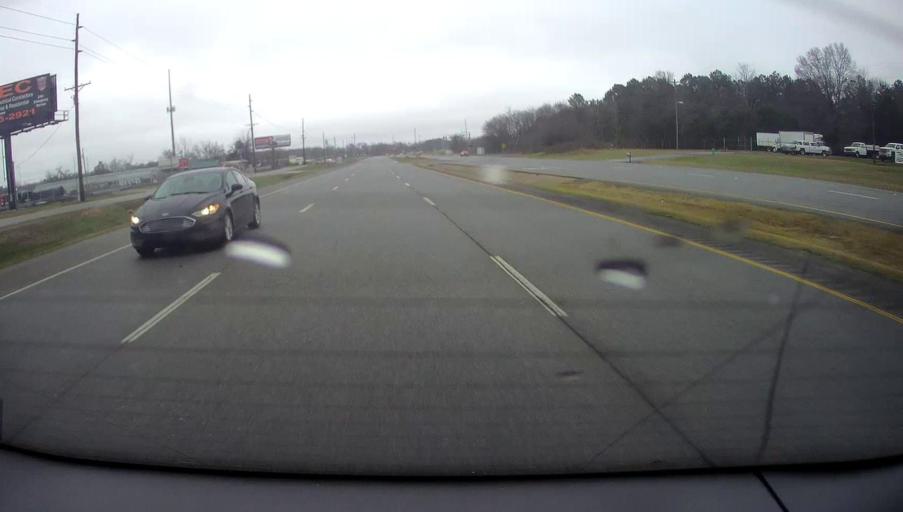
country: US
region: Alabama
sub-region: Morgan County
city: Decatur
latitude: 34.6136
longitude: -87.0312
